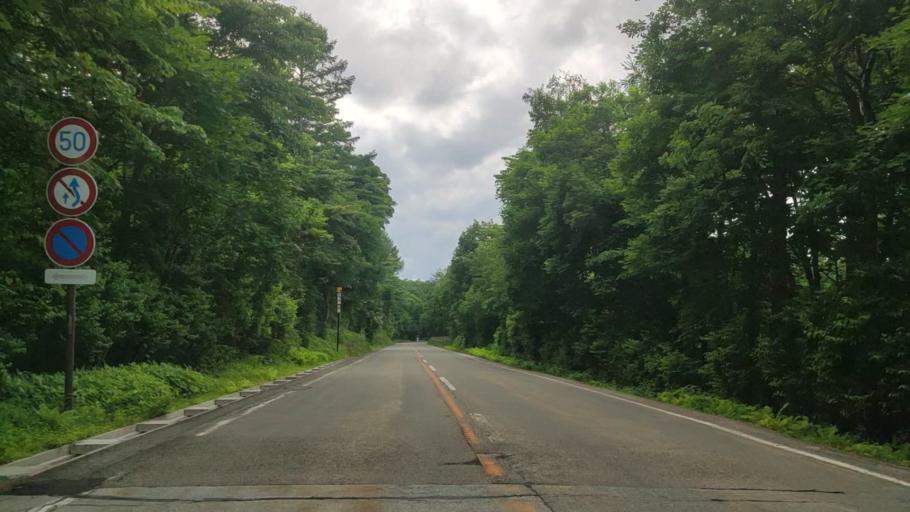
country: JP
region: Yamanashi
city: Fujikawaguchiko
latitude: 35.4223
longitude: 138.7377
